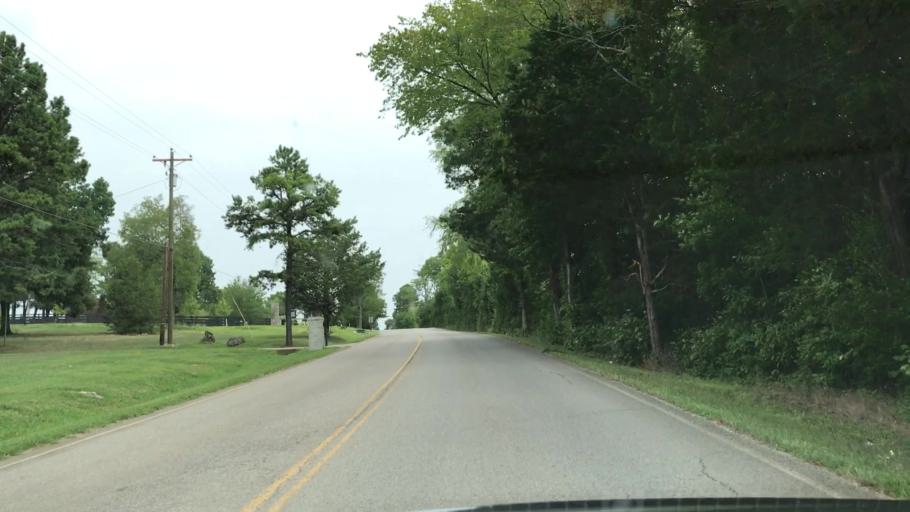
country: US
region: Tennessee
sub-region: Williamson County
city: Nolensville
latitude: 35.9543
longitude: -86.6345
